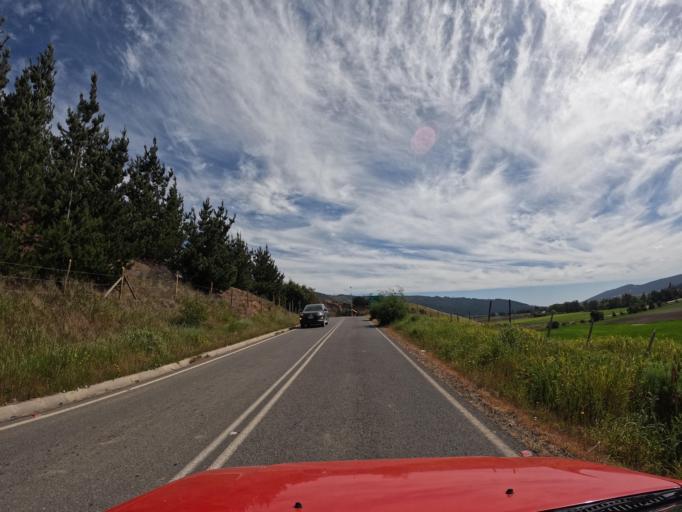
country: CL
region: Maule
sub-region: Provincia de Talca
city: Constitucion
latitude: -35.0404
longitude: -72.0601
